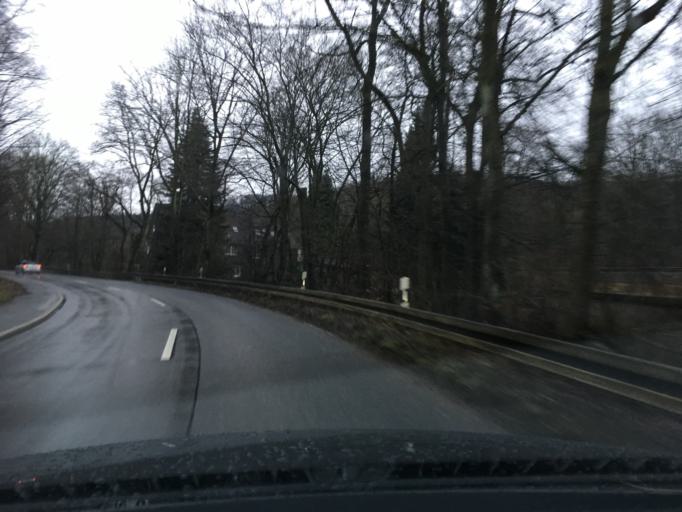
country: DE
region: North Rhine-Westphalia
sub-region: Regierungsbezirk Dusseldorf
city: Velbert
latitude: 51.3217
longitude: 7.0841
